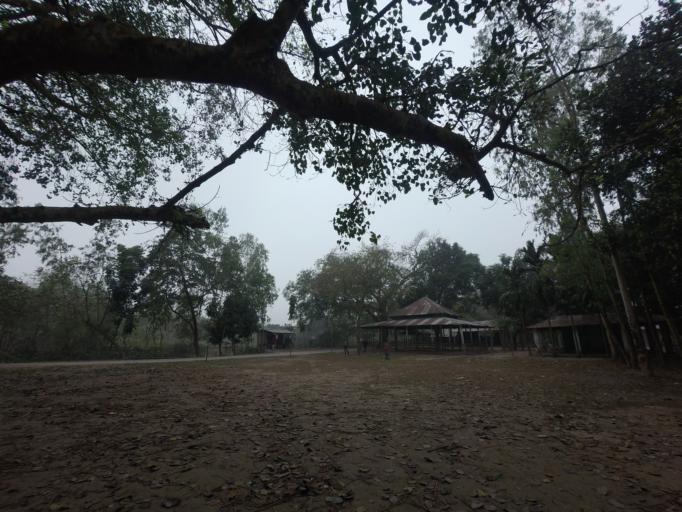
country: BD
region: Rajshahi
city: Saidpur
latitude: 26.0453
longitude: 88.8739
